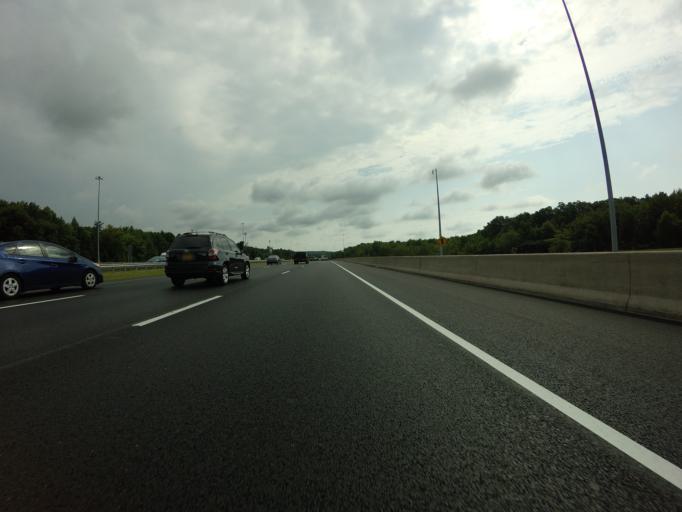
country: US
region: Maryland
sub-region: Harford County
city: Aberdeen
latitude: 39.5275
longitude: -76.1892
